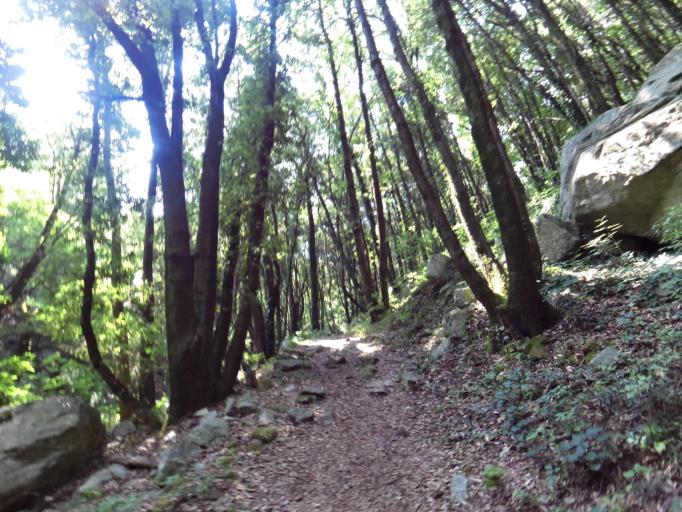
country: IT
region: Calabria
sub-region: Provincia di Reggio Calabria
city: Bivongi
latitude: 38.4995
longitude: 16.3982
